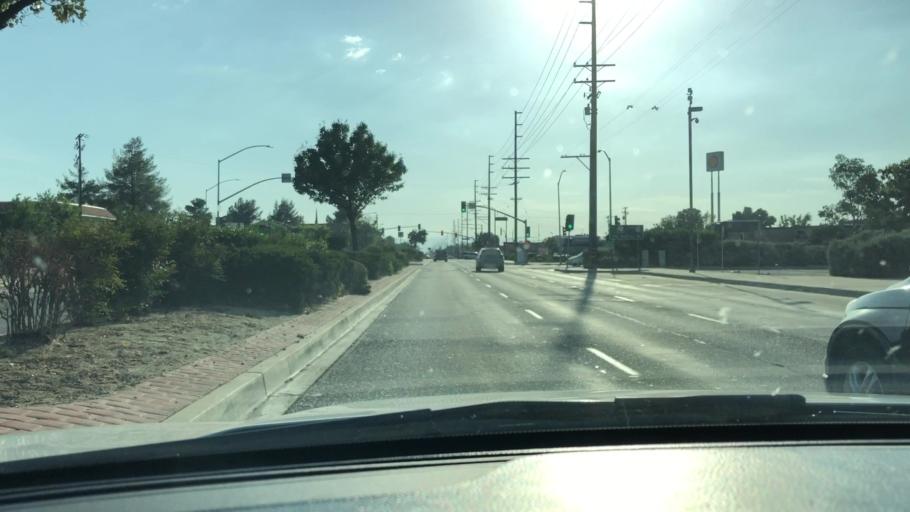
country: US
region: California
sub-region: Los Angeles County
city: Lancaster
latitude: 34.6750
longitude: -118.1590
